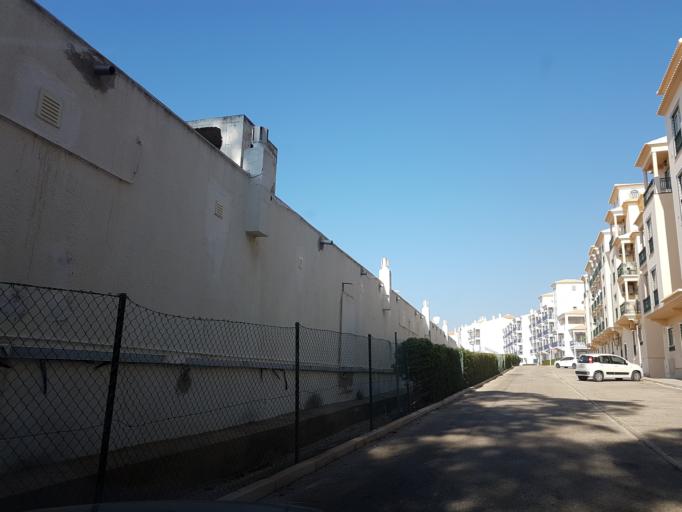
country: PT
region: Faro
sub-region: Albufeira
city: Albufeira
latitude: 37.0872
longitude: -8.2229
